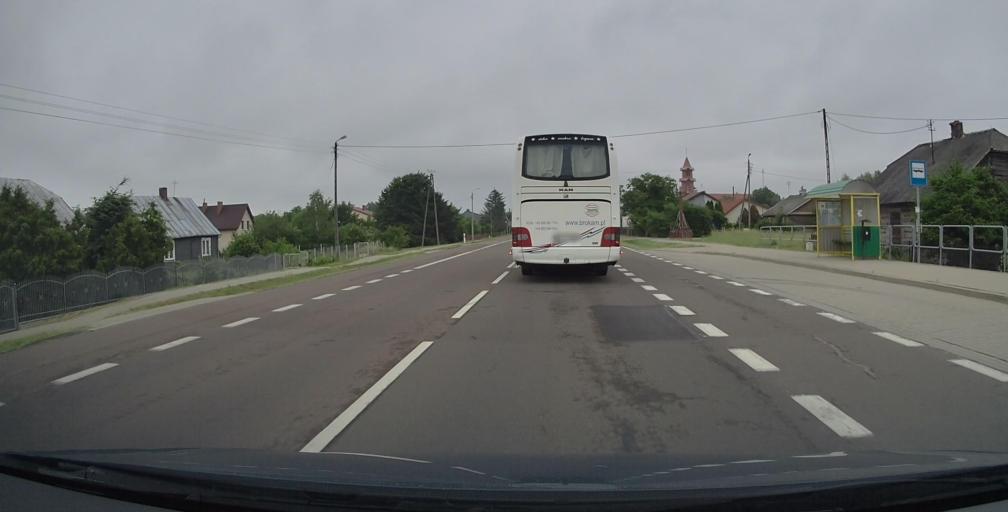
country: PL
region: Lublin Voivodeship
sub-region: Powiat bialski
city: Zalesie
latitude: 52.0373
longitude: 23.4853
